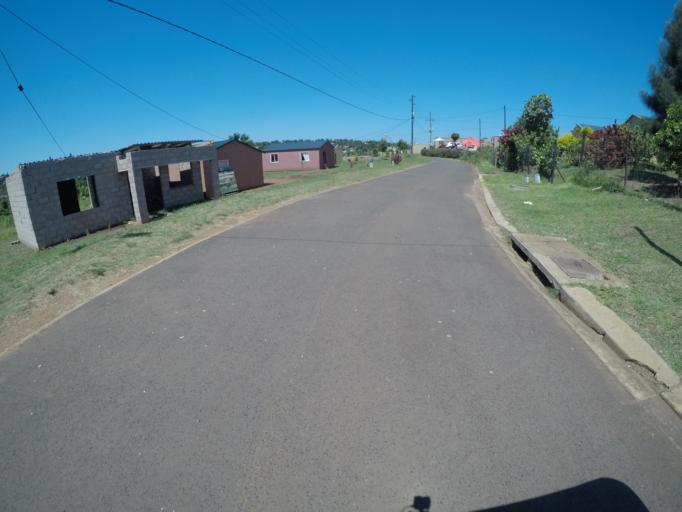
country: ZA
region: KwaZulu-Natal
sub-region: uThungulu District Municipality
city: Empangeni
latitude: -28.7640
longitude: 31.8810
